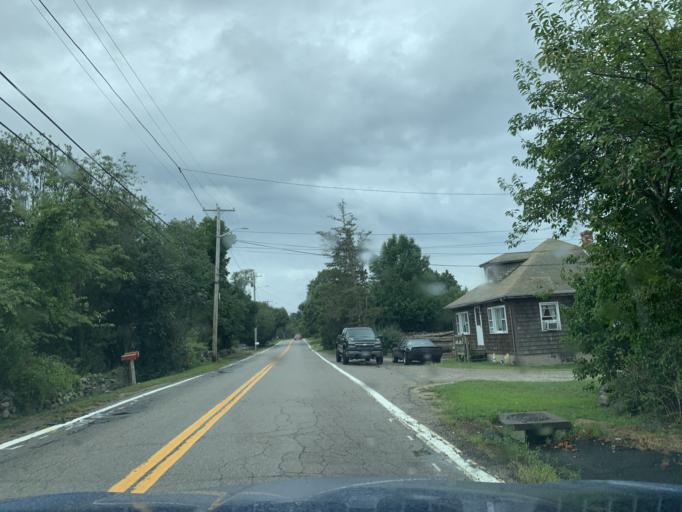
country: US
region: Rhode Island
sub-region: Bristol County
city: Warren
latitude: 41.7426
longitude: -71.2660
